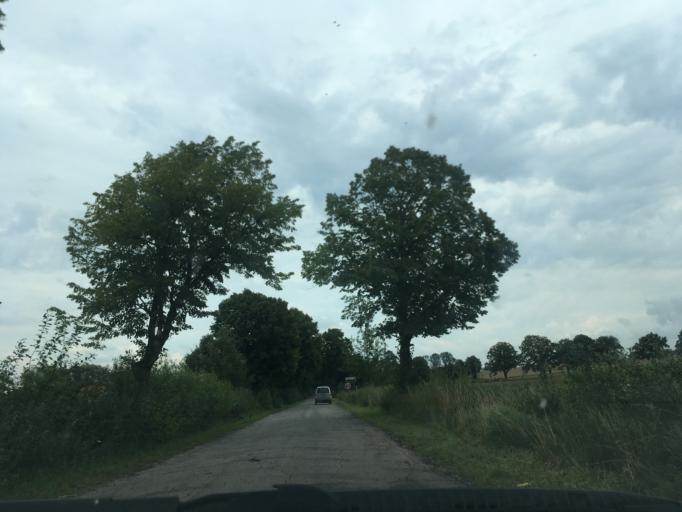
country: PL
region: Warmian-Masurian Voivodeship
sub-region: Powiat wegorzewski
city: Pozezdrze
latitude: 54.1419
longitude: 21.7802
